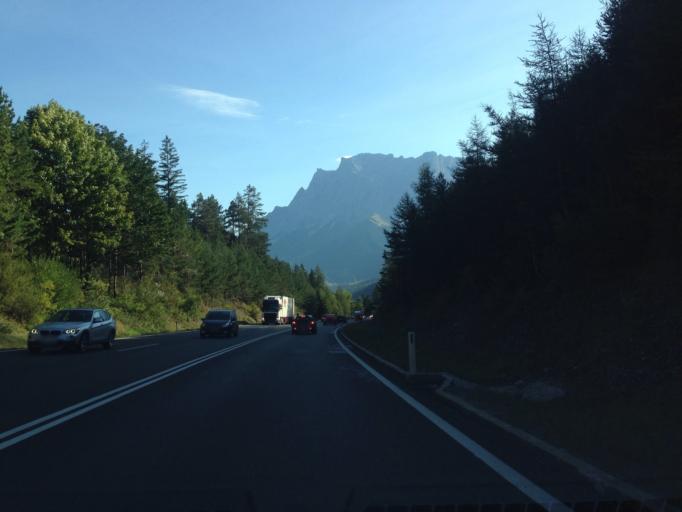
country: AT
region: Tyrol
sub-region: Politischer Bezirk Reutte
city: Biberwier
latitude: 47.3688
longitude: 10.8742
